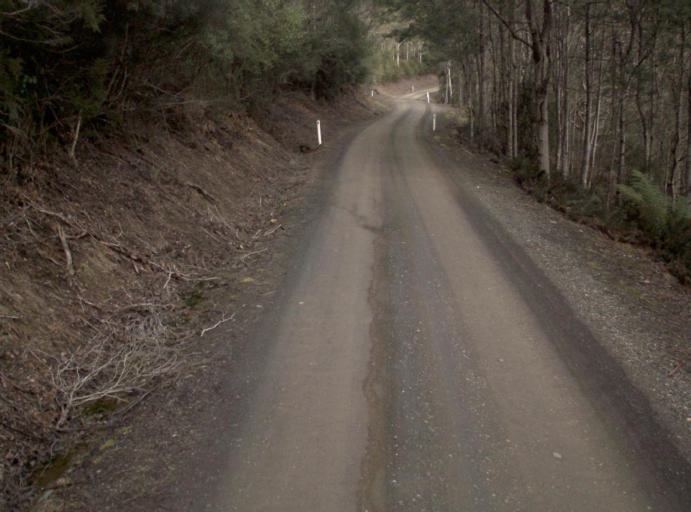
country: AU
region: Tasmania
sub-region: Dorset
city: Scottsdale
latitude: -41.2839
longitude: 147.3392
